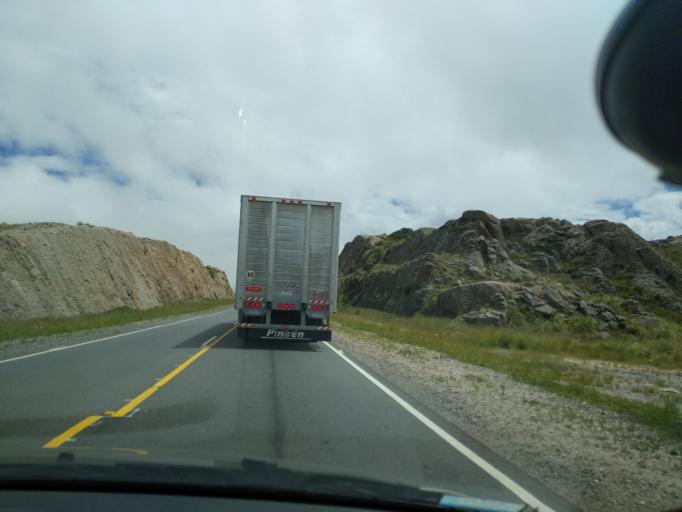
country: AR
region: Cordoba
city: Mina Clavero
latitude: -31.6425
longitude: -64.9048
